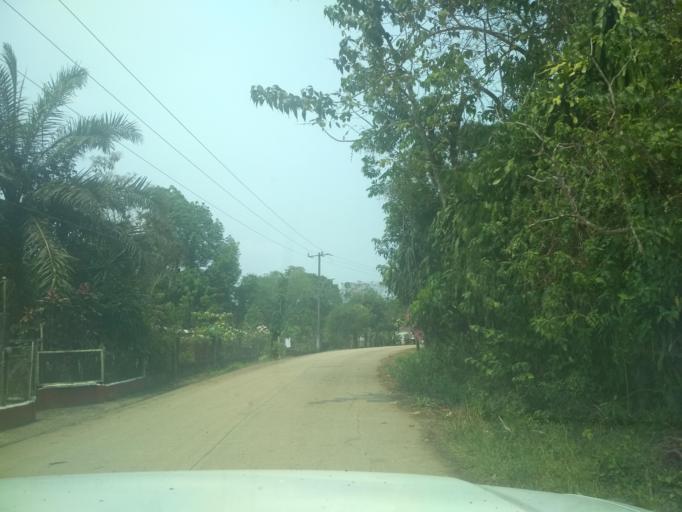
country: MX
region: Veracruz
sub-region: Tezonapa
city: Laguna Chica (Pueblo Nuevo)
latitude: 18.5158
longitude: -96.7761
